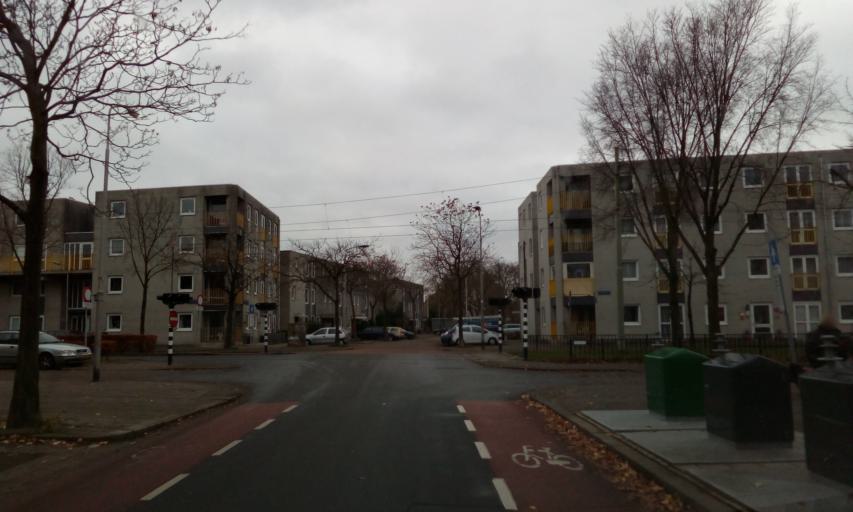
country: NL
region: South Holland
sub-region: Gemeente Delft
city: Delft
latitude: 51.9807
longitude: 4.3477
